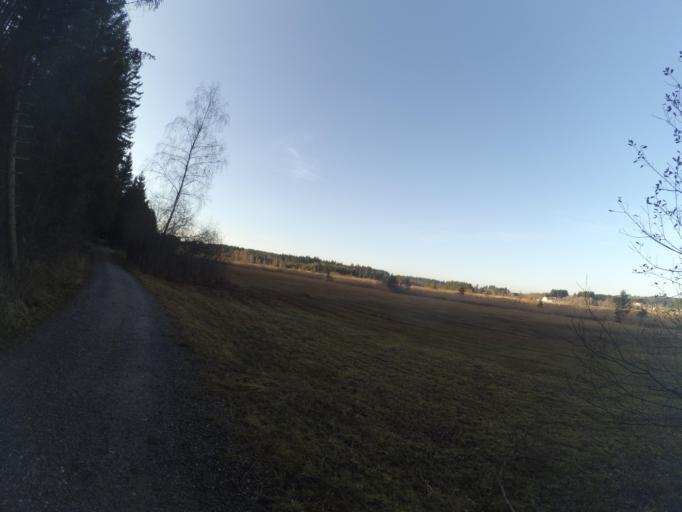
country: DE
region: Bavaria
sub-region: Swabia
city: Aitrang
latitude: 47.7961
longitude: 10.5506
